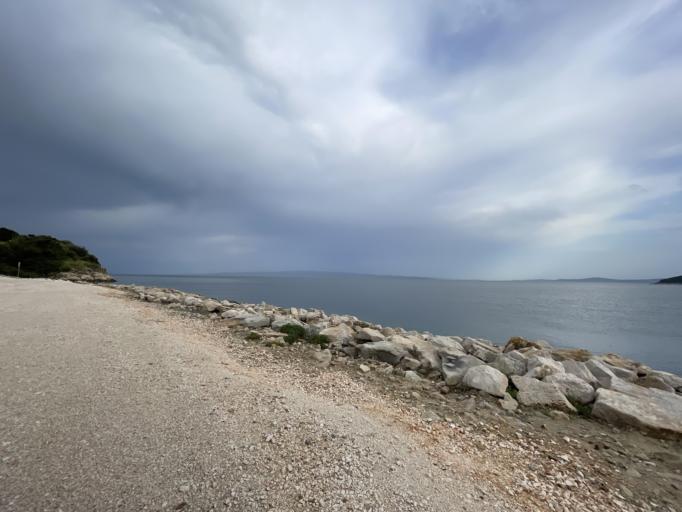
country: HR
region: Splitsko-Dalmatinska
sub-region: Grad Split
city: Split
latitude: 43.5051
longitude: 16.3998
